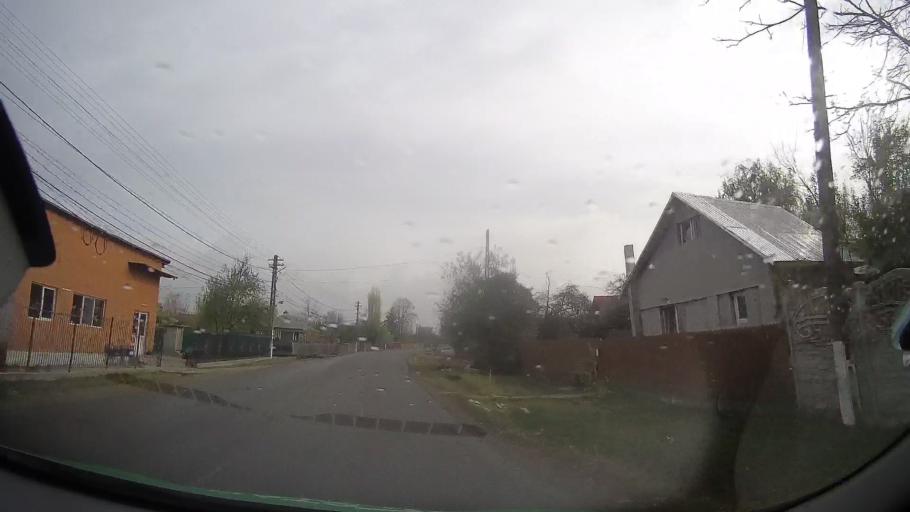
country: RO
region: Prahova
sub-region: Comuna Rafov
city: Palanca
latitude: 44.8441
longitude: 26.2347
